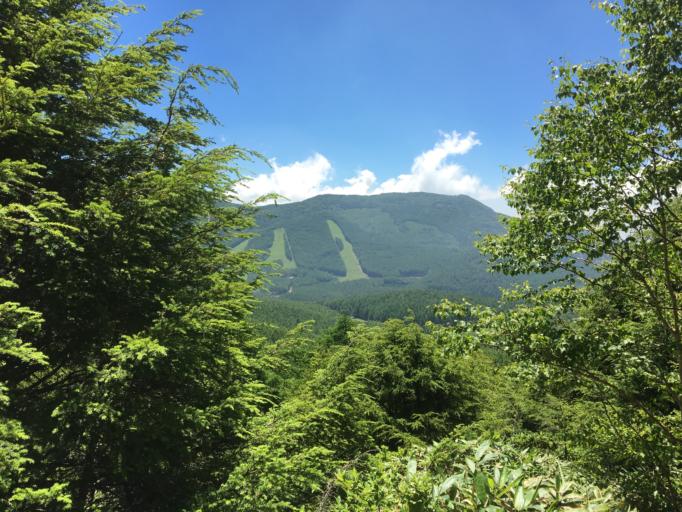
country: JP
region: Nagano
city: Komoro
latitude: 36.4333
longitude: 138.4057
